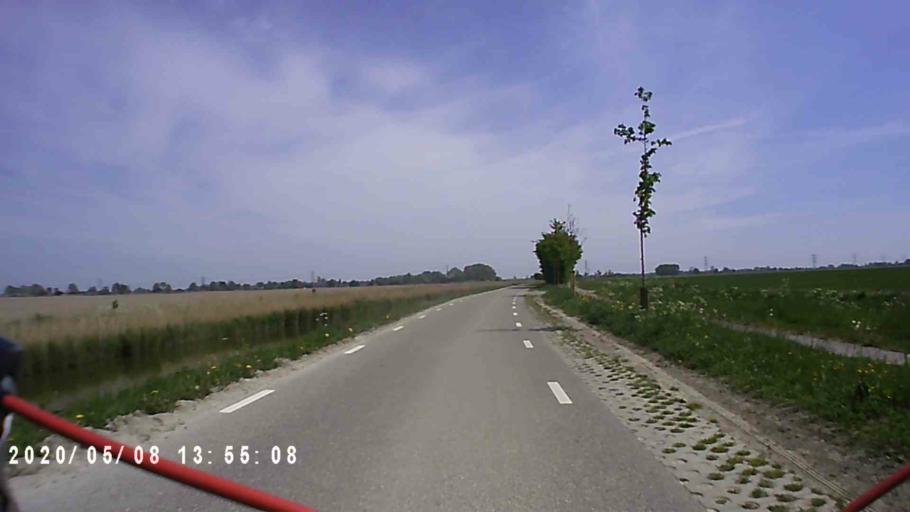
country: NL
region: Groningen
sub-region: Gemeente Appingedam
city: Appingedam
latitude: 53.3360
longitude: 6.7917
